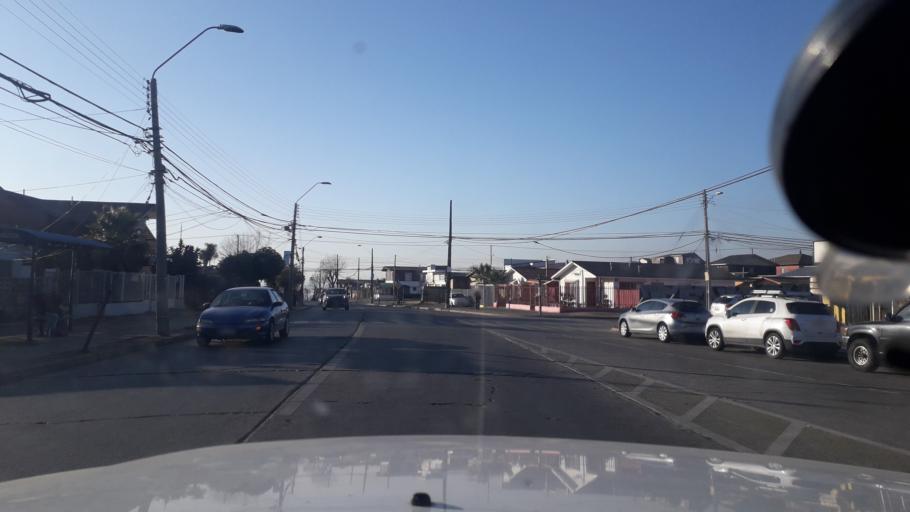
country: CL
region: Valparaiso
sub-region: Provincia de Valparaiso
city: Vina del Mar
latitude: -32.9269
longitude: -71.5167
